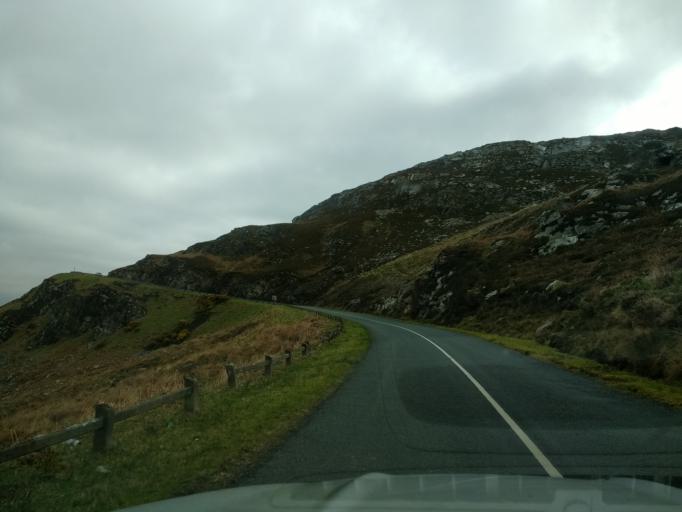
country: IE
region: Ulster
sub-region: County Donegal
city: Ramelton
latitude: 55.1824
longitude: -7.5979
